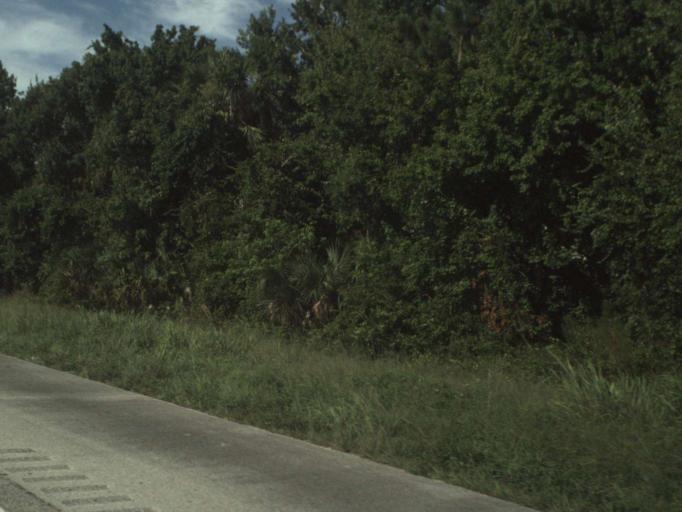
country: US
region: Florida
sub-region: Indian River County
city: Fellsmere
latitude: 27.7549
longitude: -80.5517
